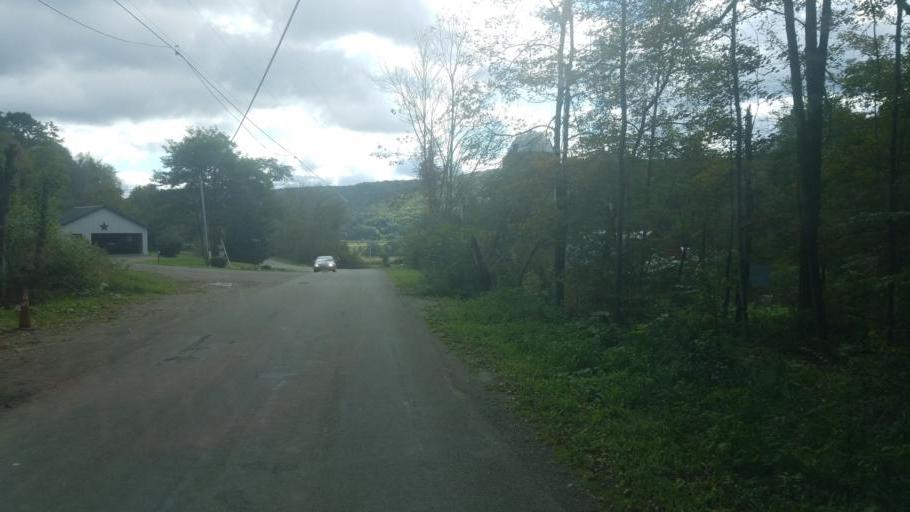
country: US
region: New York
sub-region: Allegany County
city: Cuba
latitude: 42.2184
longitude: -78.3298
